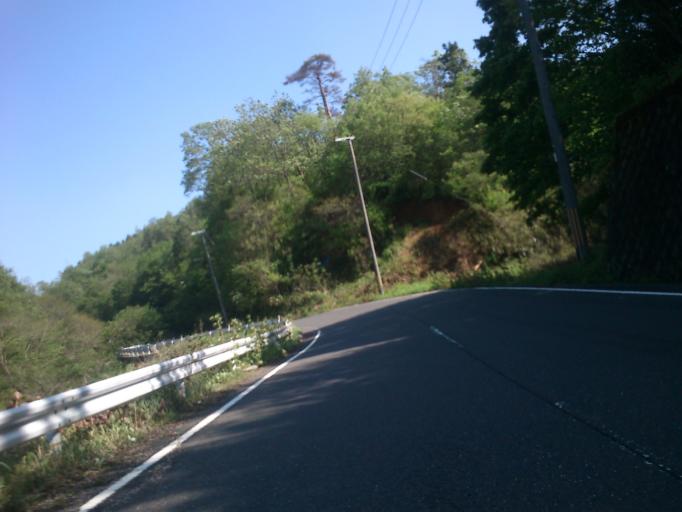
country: JP
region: Kyoto
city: Miyazu
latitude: 35.6218
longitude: 135.1276
